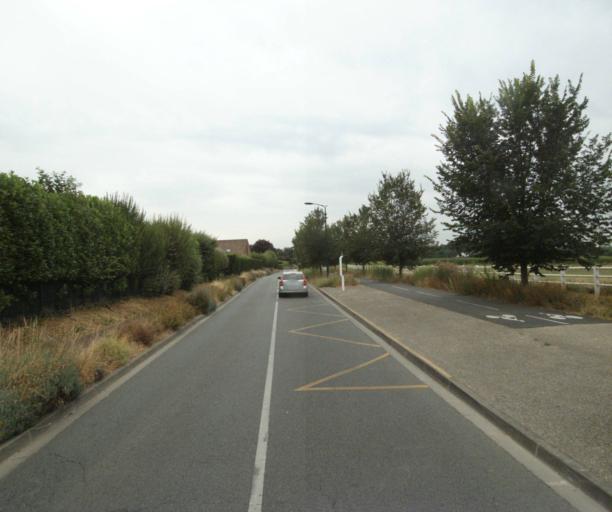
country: FR
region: Nord-Pas-de-Calais
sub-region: Departement du Nord
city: Bondues
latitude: 50.7005
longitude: 3.0867
